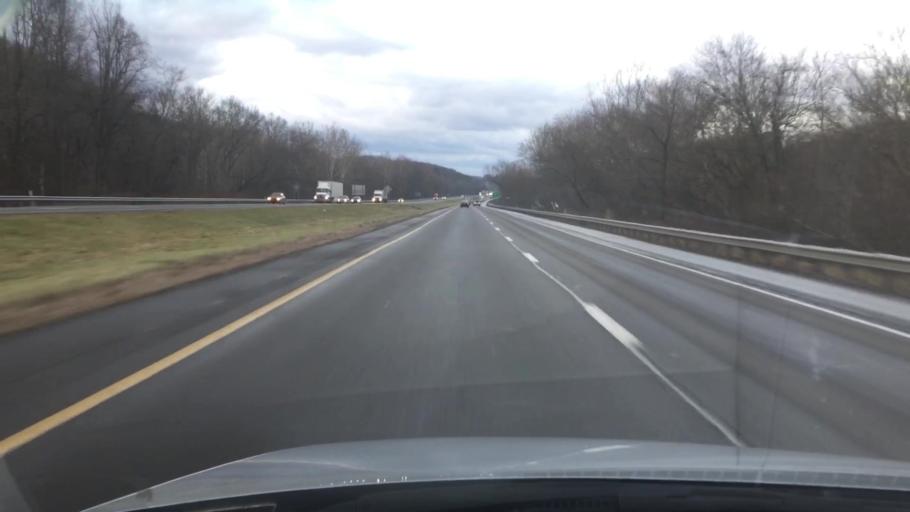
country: US
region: Pennsylvania
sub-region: Columbia County
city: Light Street
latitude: 41.0265
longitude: -76.4438
